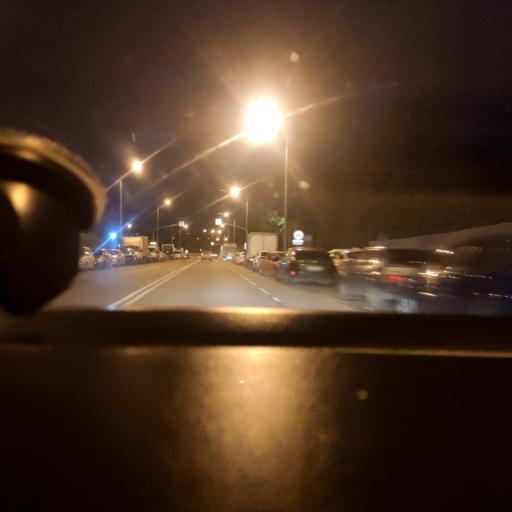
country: RU
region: Moskovskaya
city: Oktyabr'skiy
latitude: 55.6239
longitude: 37.9498
